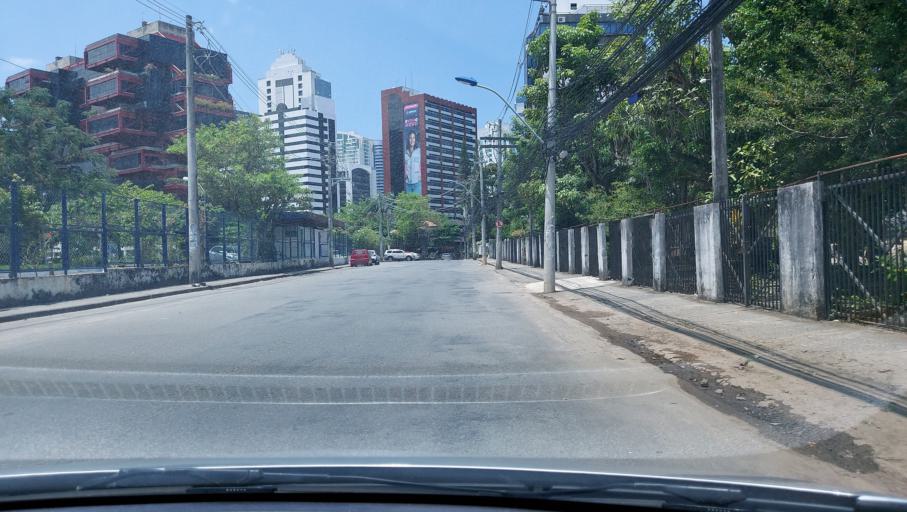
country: BR
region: Bahia
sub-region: Salvador
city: Salvador
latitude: -12.9806
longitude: -38.4579
